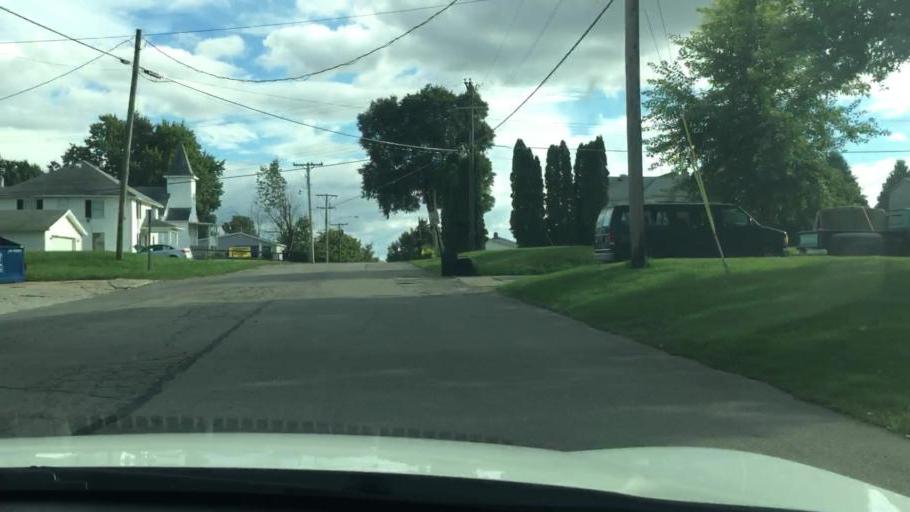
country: US
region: Ohio
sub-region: Champaign County
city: Mechanicsburg
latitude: 40.0814
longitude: -83.5656
